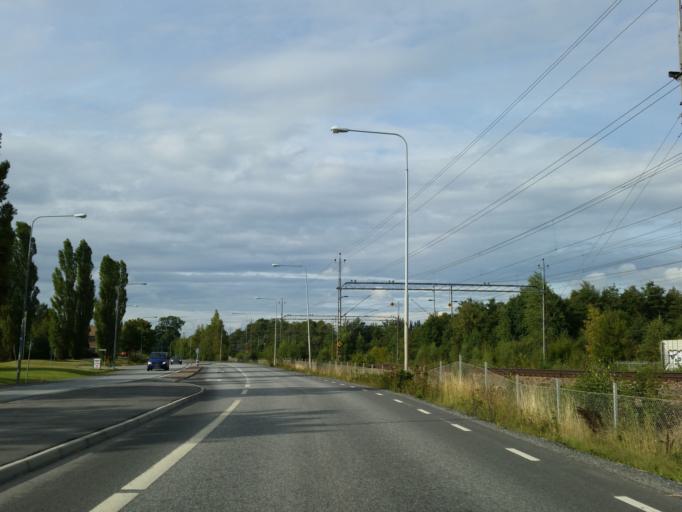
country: SE
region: Stockholm
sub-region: Sollentuna Kommun
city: Sollentuna
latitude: 59.4625
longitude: 17.9234
